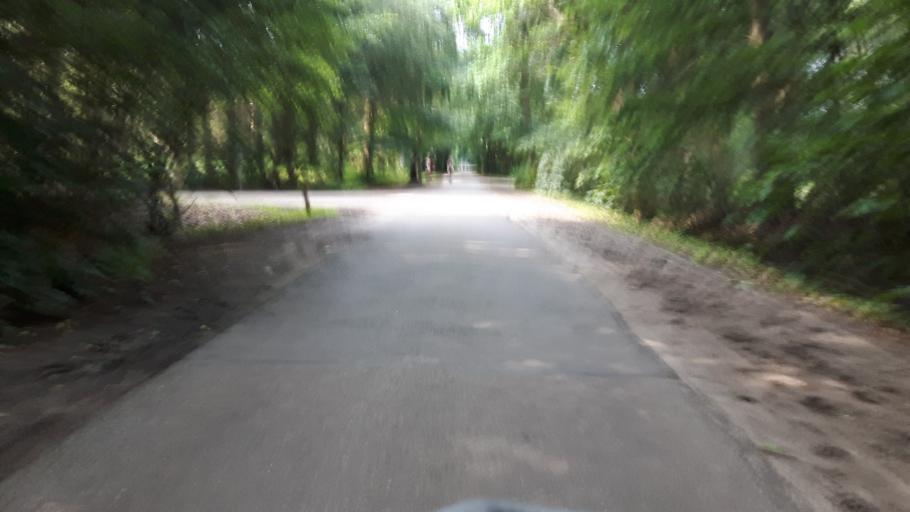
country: NL
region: Utrecht
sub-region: Gemeente Soest
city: Soest
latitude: 52.1569
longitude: 5.2833
